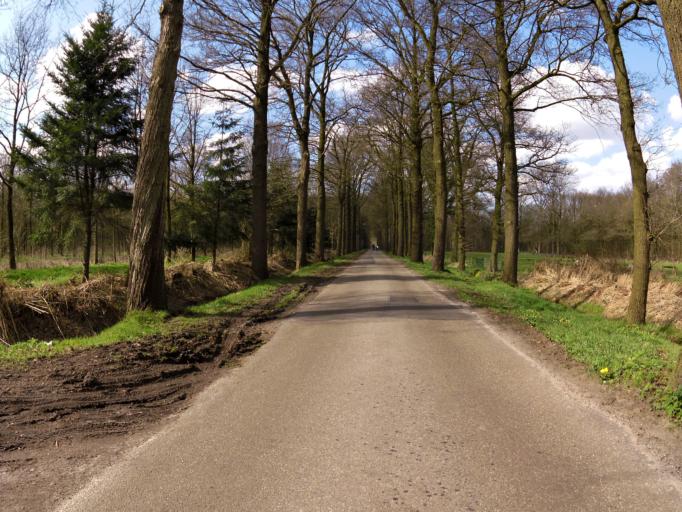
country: NL
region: North Brabant
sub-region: Gemeente Oisterwijk
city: Oisterwijk
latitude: 51.6312
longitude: 5.1752
